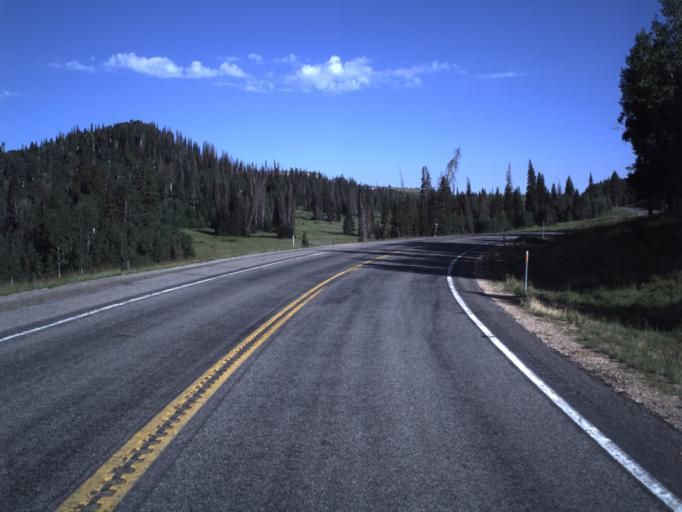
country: US
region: Utah
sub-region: Sanpete County
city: Fairview
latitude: 39.5957
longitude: -111.2695
